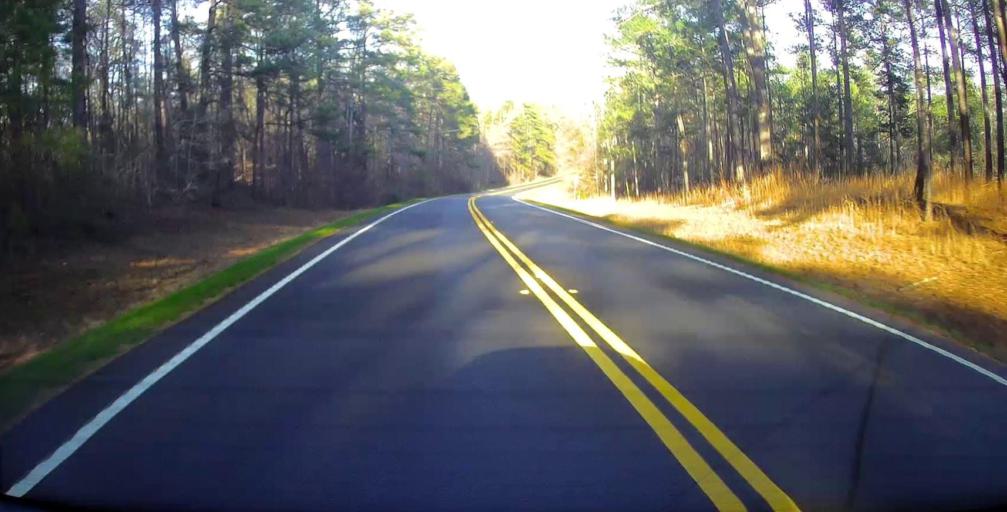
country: US
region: Georgia
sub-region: Harris County
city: Hamilton
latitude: 32.7486
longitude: -84.9378
